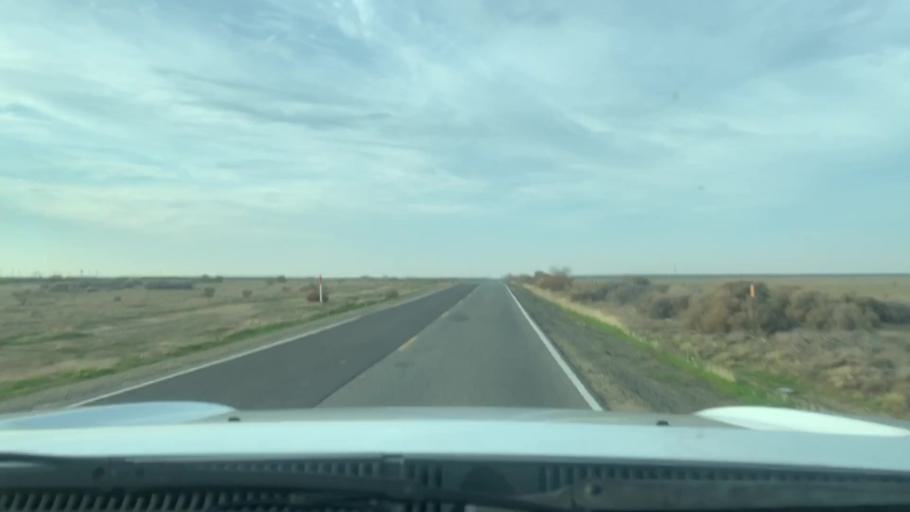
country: US
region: California
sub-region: Kern County
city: Lost Hills
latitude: 35.5483
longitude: -119.7854
